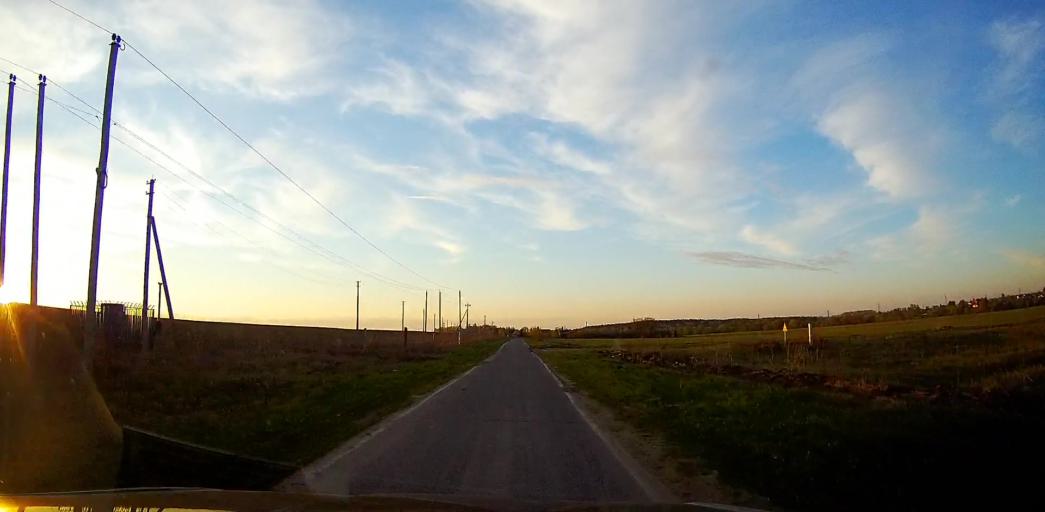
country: RU
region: Moskovskaya
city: Peski
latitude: 55.2220
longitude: 38.7368
